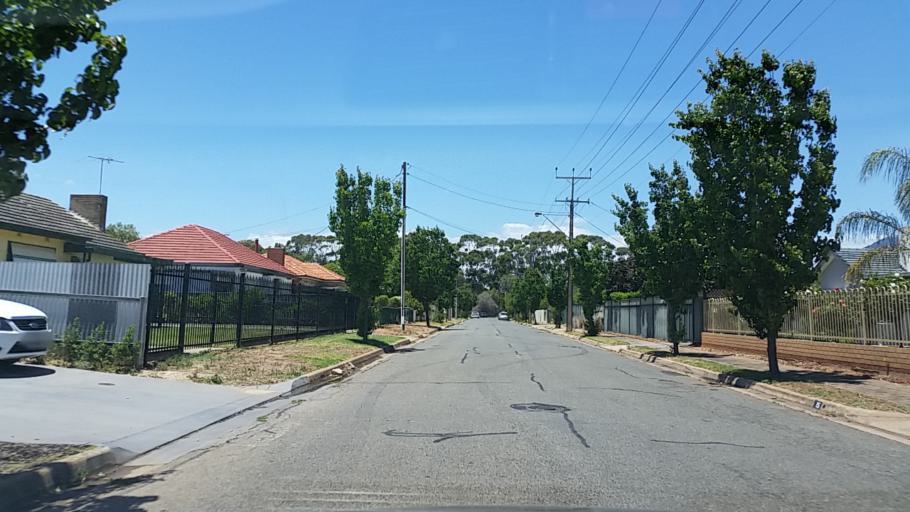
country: AU
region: South Australia
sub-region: Salisbury
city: Salisbury
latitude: -34.7668
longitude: 138.6397
